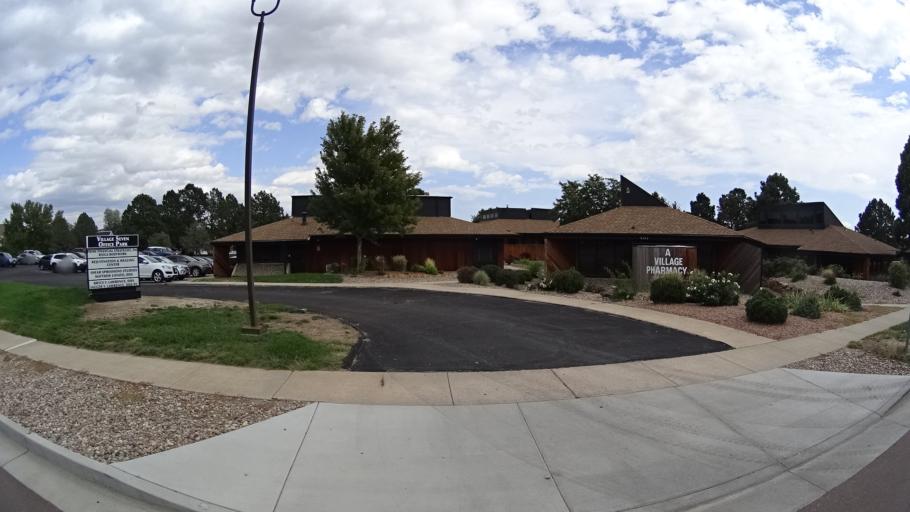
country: US
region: Colorado
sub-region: El Paso County
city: Cimarron Hills
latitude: 38.8791
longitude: -104.7546
